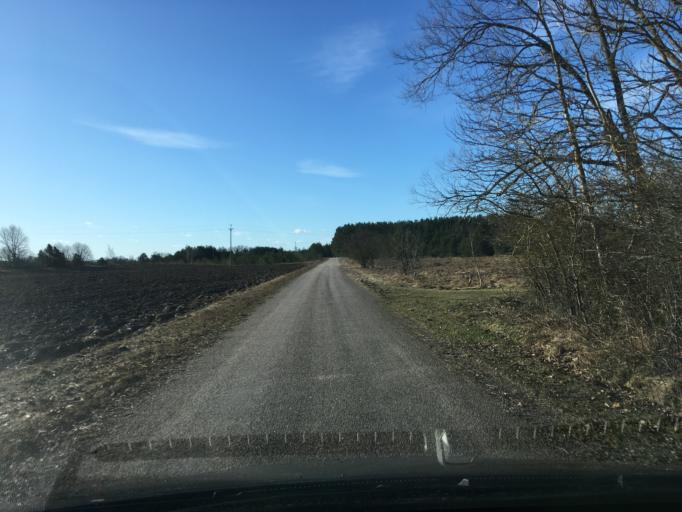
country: EE
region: Laeaene
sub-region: Lihula vald
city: Lihula
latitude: 58.5830
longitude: 23.7052
